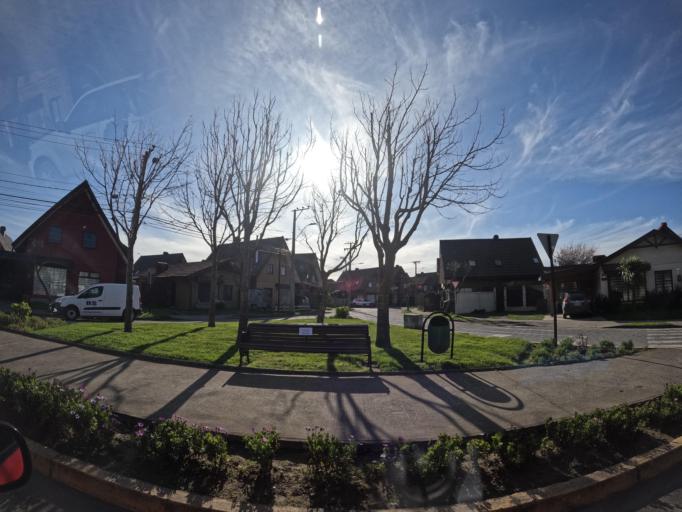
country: CL
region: Biobio
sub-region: Provincia de Concepcion
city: Talcahuano
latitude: -36.7696
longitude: -73.0771
